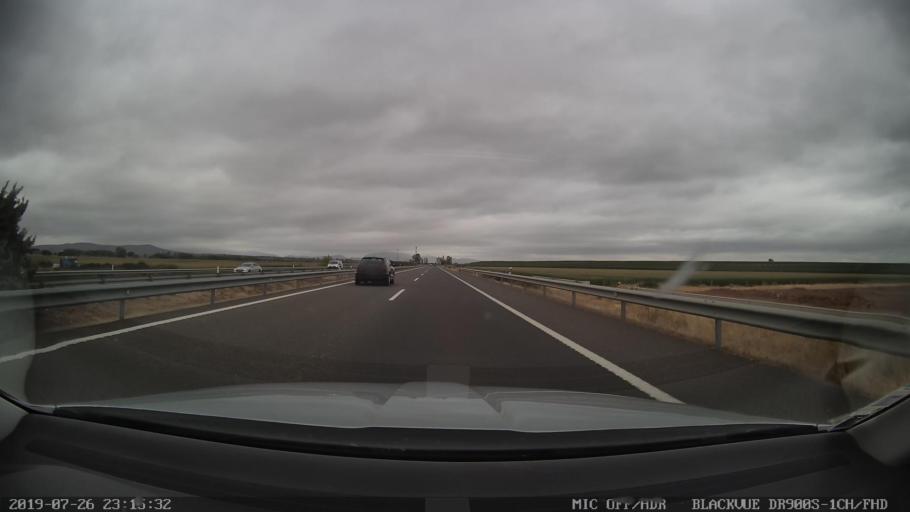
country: ES
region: Extremadura
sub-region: Provincia de Badajoz
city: Santa Amalia
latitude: 39.0547
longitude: -6.0565
